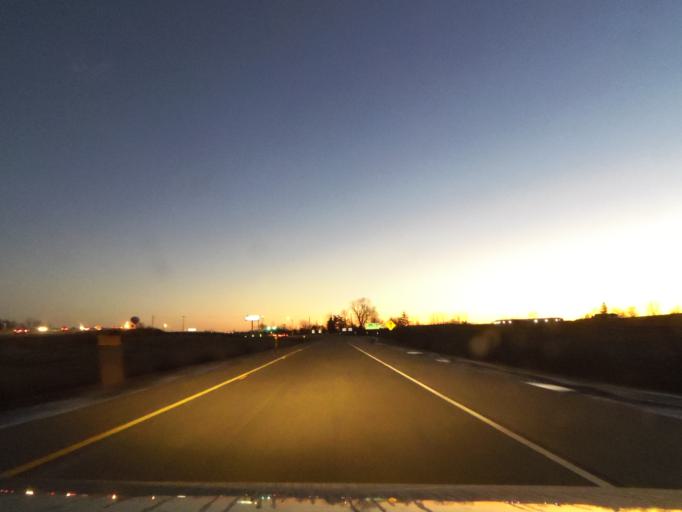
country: US
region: Indiana
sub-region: Lake County
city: Crown Point
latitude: 41.4229
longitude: -87.3220
